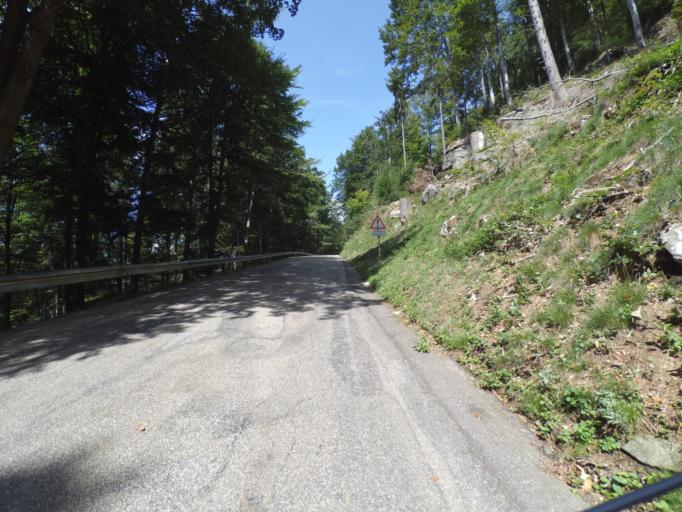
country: DE
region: Baden-Wuerttemberg
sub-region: Freiburg Region
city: Waldkirch
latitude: 48.0806
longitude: 7.9968
